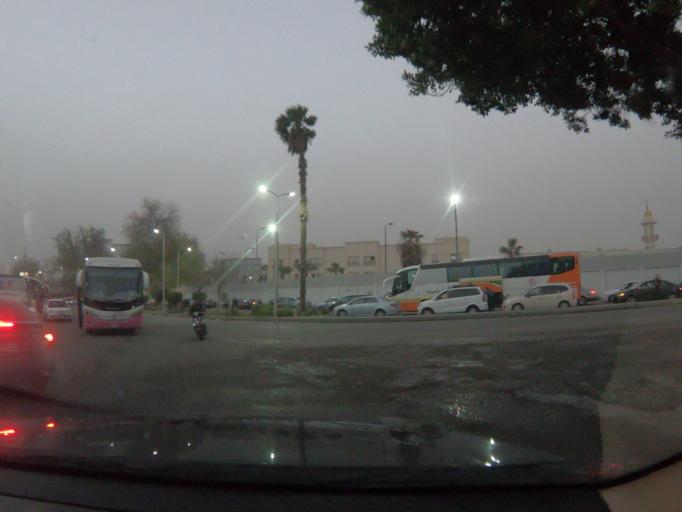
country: EG
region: Muhafazat al Qahirah
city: Cairo
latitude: 30.0899
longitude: 31.3485
